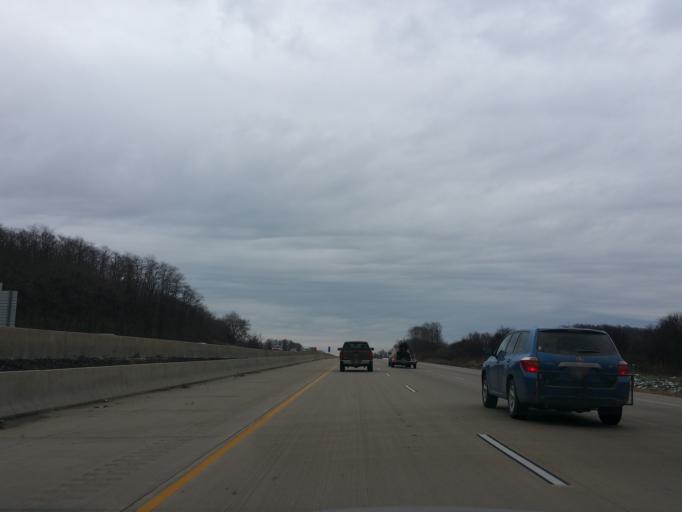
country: US
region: Wisconsin
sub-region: Columbia County
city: Lodi
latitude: 43.3211
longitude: -89.4467
